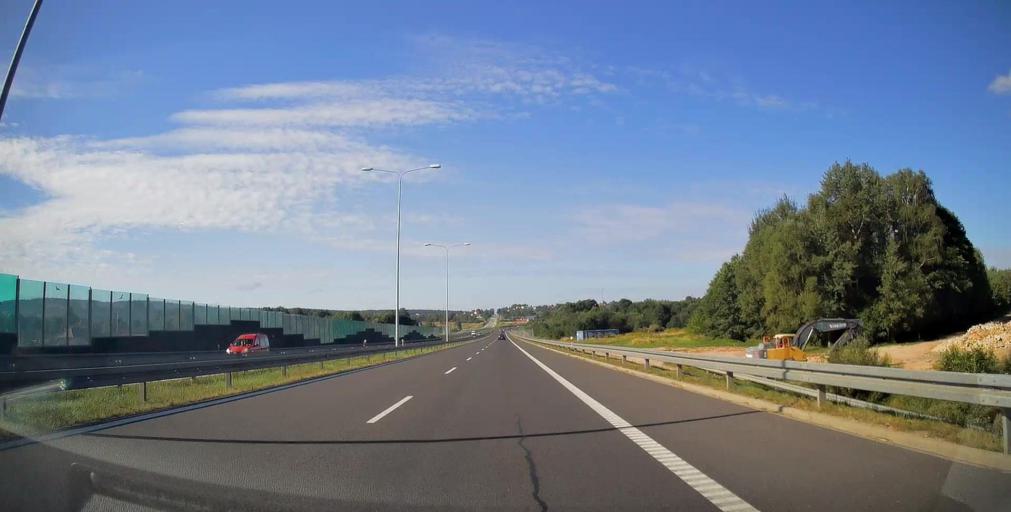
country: PL
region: Swietokrzyskie
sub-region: Powiat kielecki
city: Zagnansk
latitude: 50.9552
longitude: 20.7059
